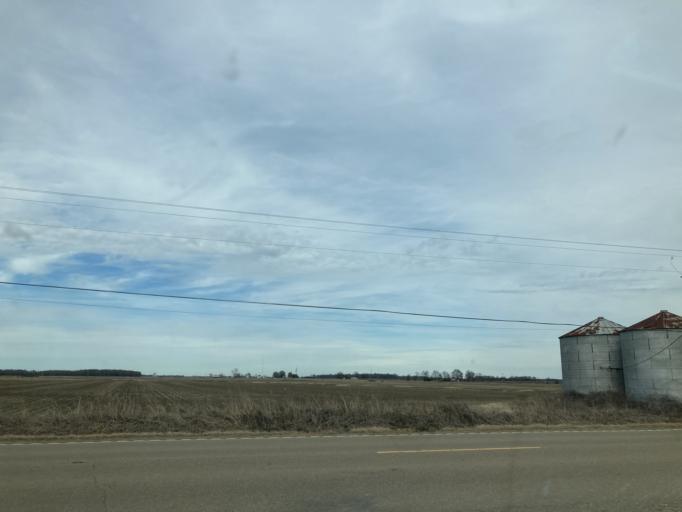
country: US
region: Mississippi
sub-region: Humphreys County
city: Belzoni
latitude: 33.1836
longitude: -90.5766
